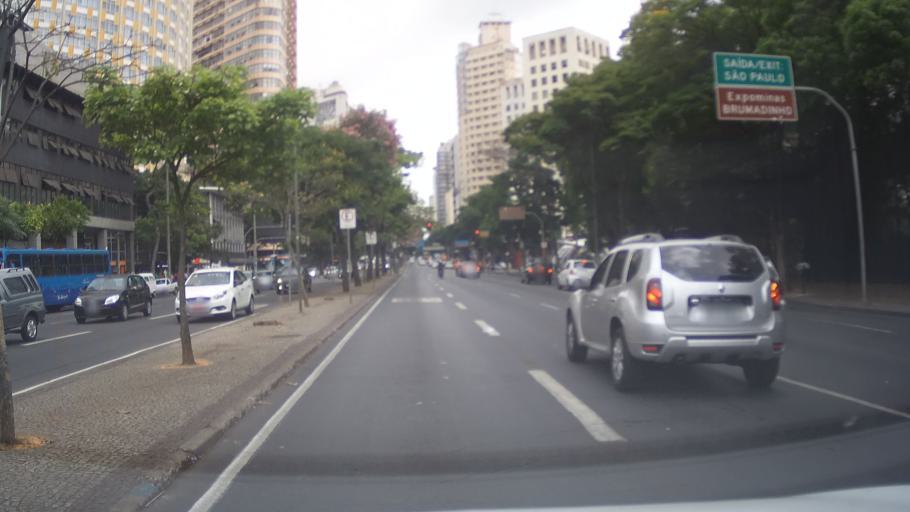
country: BR
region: Minas Gerais
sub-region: Belo Horizonte
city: Belo Horizonte
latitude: -19.9233
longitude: -43.9360
